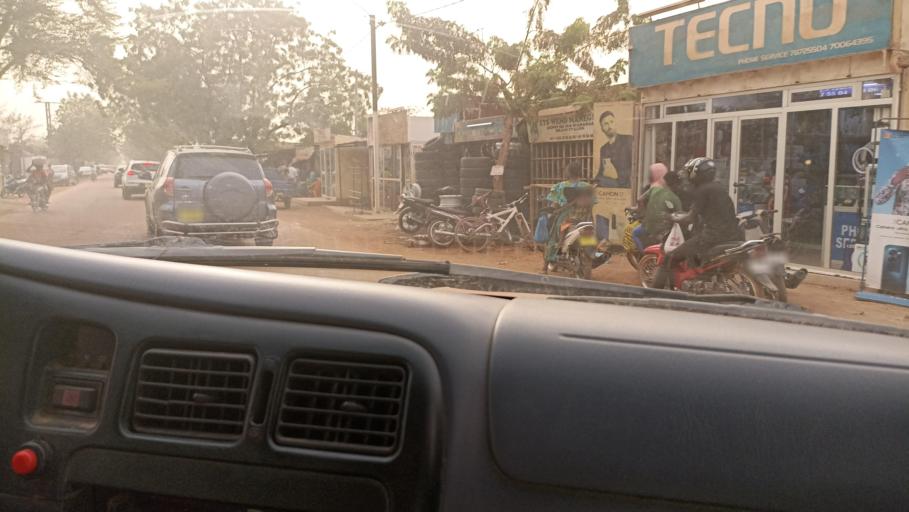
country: BF
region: Centre
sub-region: Kadiogo Province
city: Ouagadougou
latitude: 12.3813
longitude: -1.5403
